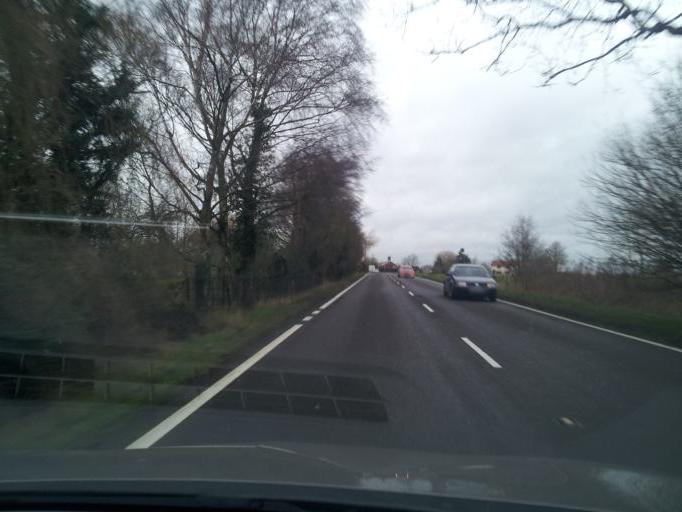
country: GB
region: England
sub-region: Suffolk
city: Botesdale
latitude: 52.3289
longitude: 0.9340
